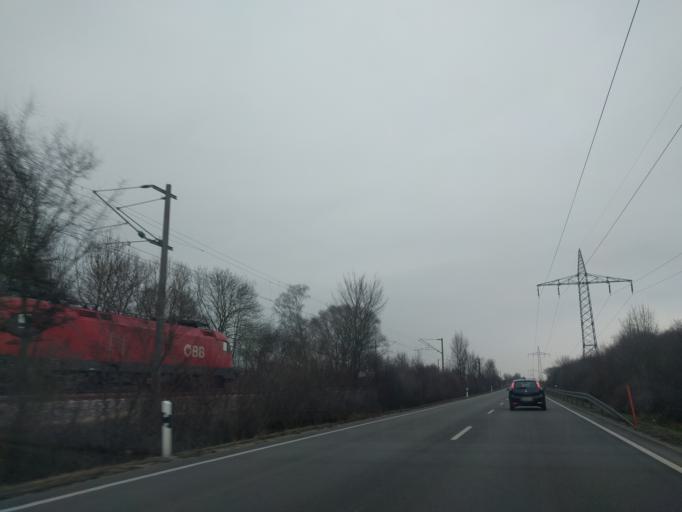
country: DE
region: Bavaria
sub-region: Swabia
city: Asbach-Baumenheim
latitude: 48.6926
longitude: 10.8302
